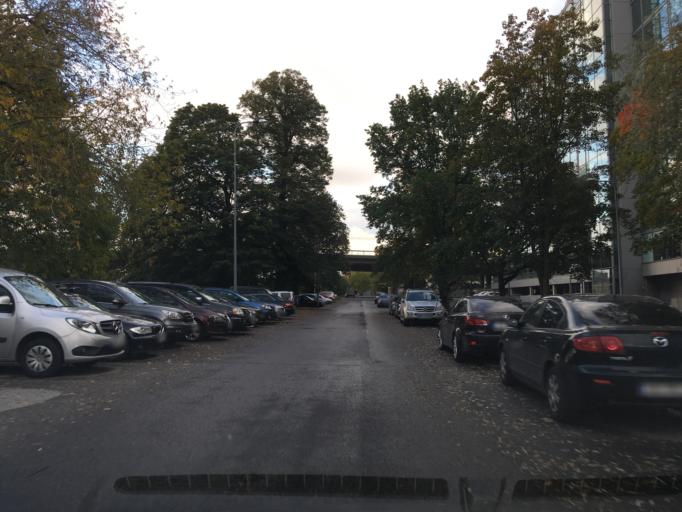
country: EE
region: Harju
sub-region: Tallinna linn
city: Tallinn
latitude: 59.4196
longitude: 24.7393
